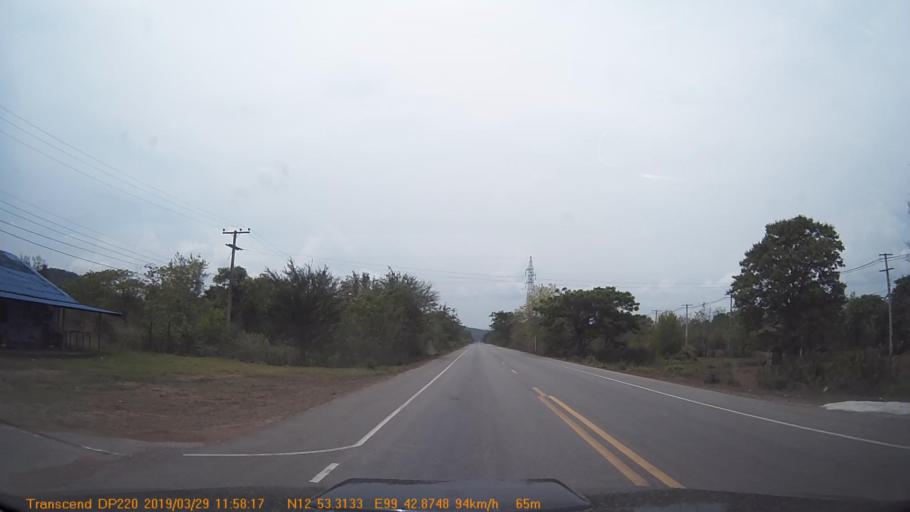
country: TH
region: Phetchaburi
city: Kaeng Krachan
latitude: 12.8882
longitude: 99.7144
